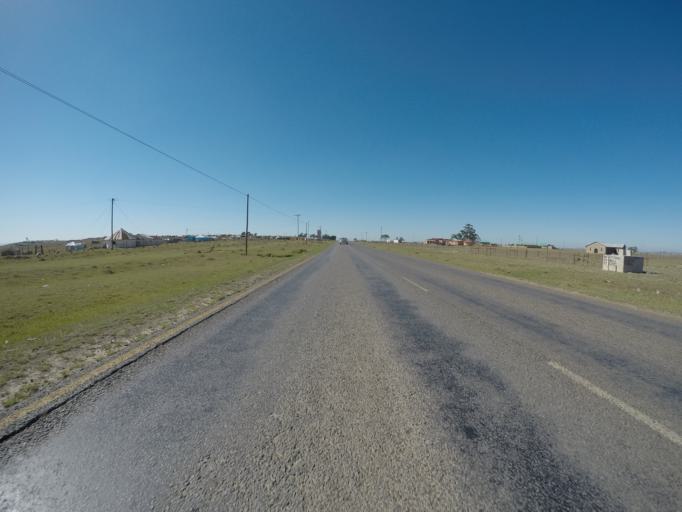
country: ZA
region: Eastern Cape
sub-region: OR Tambo District Municipality
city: Mthatha
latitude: -31.7844
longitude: 28.7410
